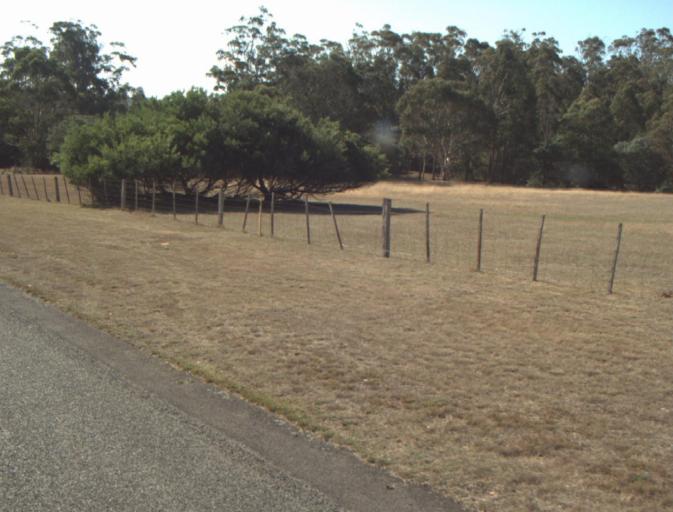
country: AU
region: Tasmania
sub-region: Launceston
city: Mayfield
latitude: -41.3244
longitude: 147.0546
